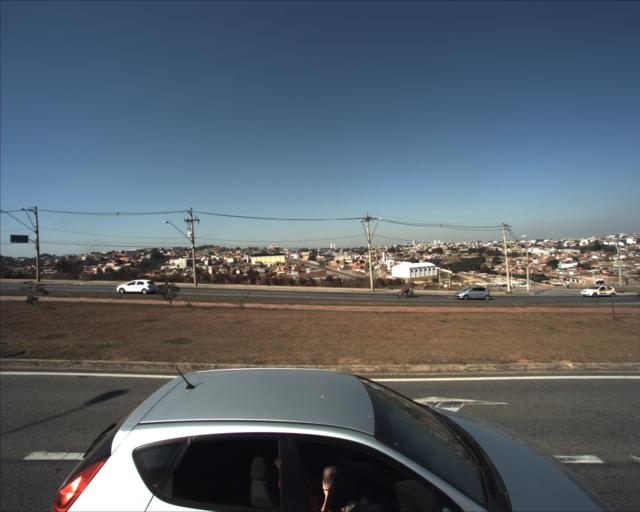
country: BR
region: Sao Paulo
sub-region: Sorocaba
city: Sorocaba
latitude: -23.4862
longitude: -47.4902
